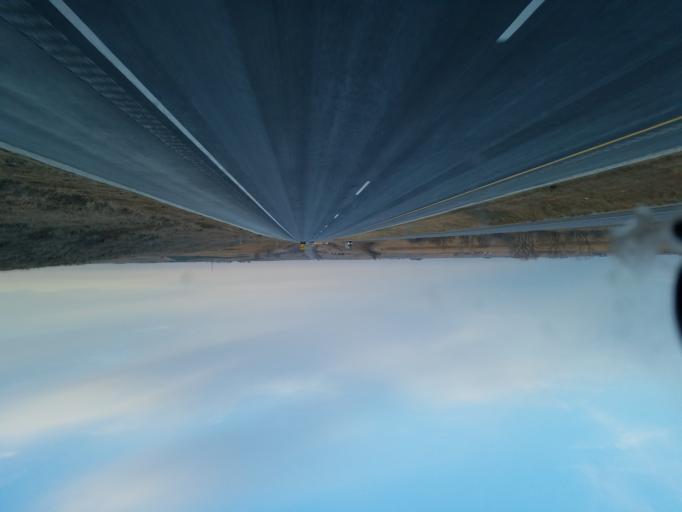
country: US
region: Iowa
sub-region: Harrison County
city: Logan
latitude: 41.4984
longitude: -95.7059
